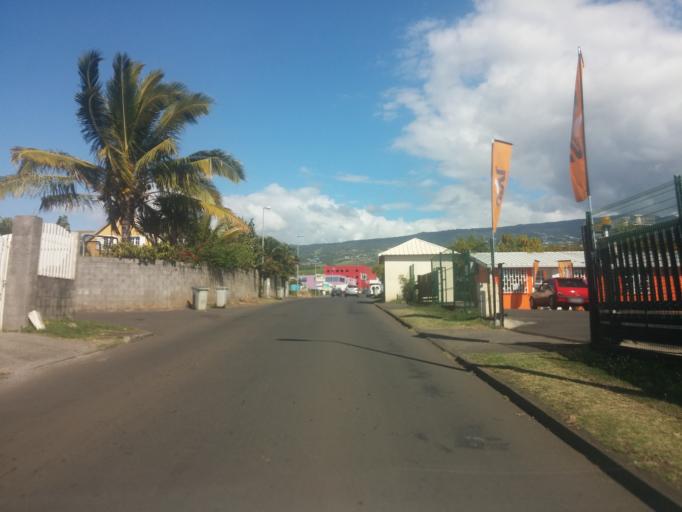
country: RE
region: Reunion
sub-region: Reunion
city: Sainte-Marie
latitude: -20.8975
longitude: 55.5335
